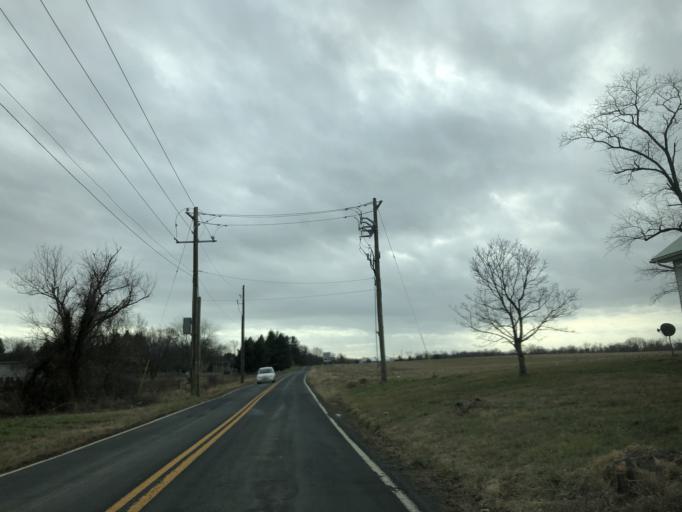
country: US
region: Maryland
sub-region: Cecil County
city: North East
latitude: 39.6752
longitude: -75.9549
